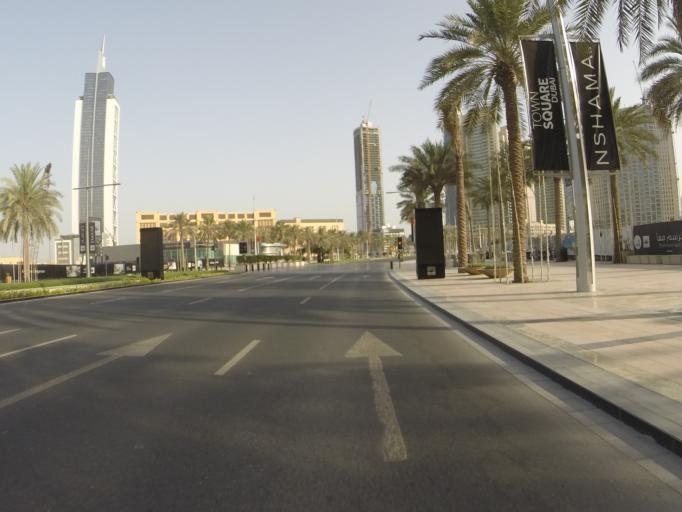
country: AE
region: Dubai
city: Dubai
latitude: 25.1928
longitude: 55.2706
